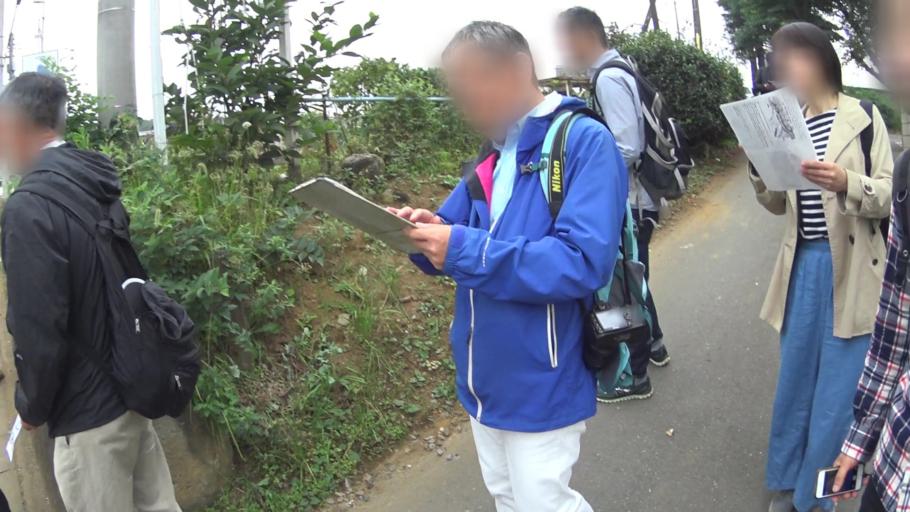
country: JP
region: Saitama
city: Hanno
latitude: 35.8607
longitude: 139.3229
